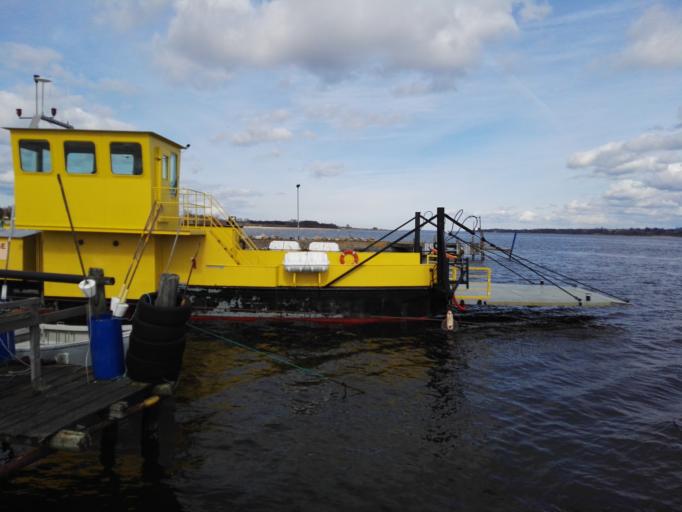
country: DK
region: Zealand
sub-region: Lejre Kommune
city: Ejby
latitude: 55.7567
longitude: 11.8363
